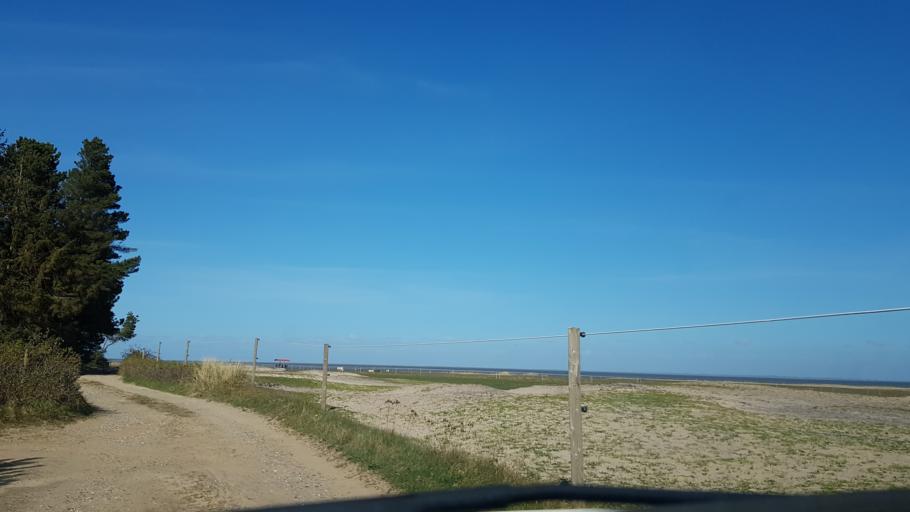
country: DE
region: Schleswig-Holstein
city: List
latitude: 55.0965
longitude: 8.5521
